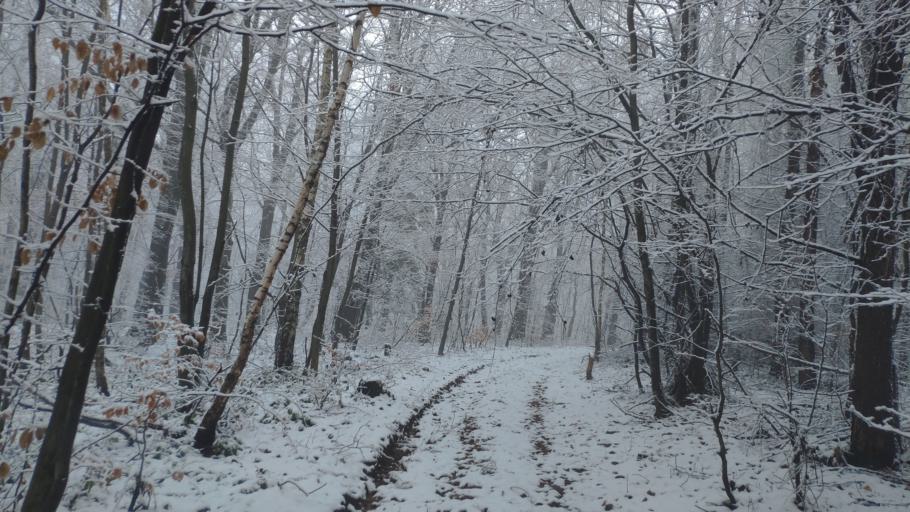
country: SK
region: Kosicky
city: Moldava nad Bodvou
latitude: 48.7383
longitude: 21.0962
